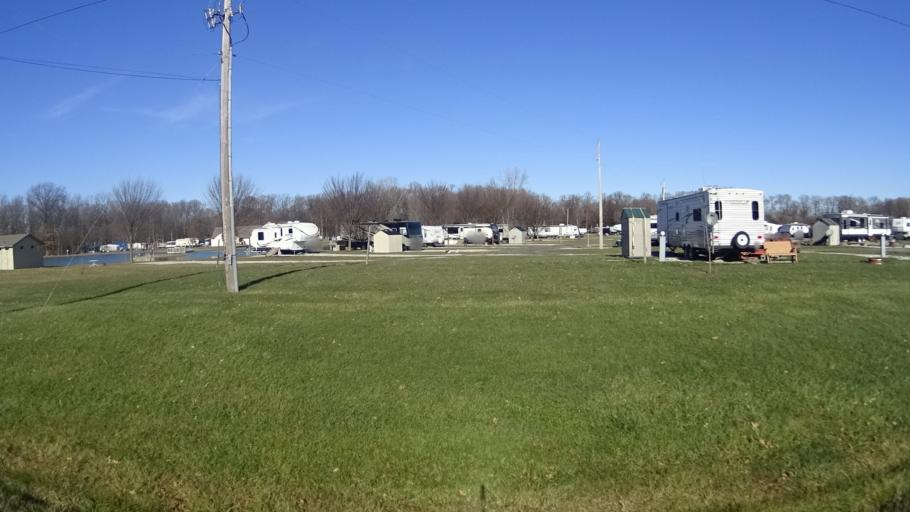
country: US
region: Ohio
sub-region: Lorain County
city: South Amherst
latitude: 41.3533
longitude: -82.3223
